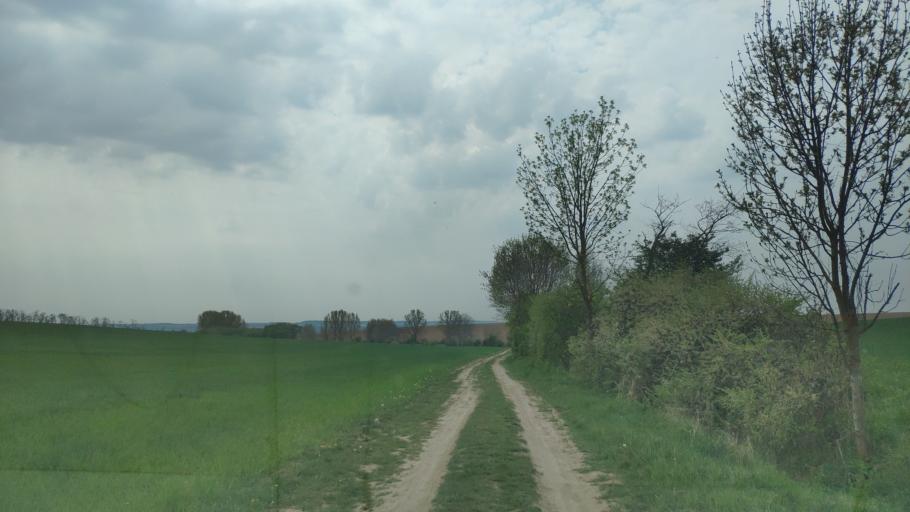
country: SK
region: Kosicky
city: Moldava nad Bodvou
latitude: 48.6173
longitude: 21.0405
